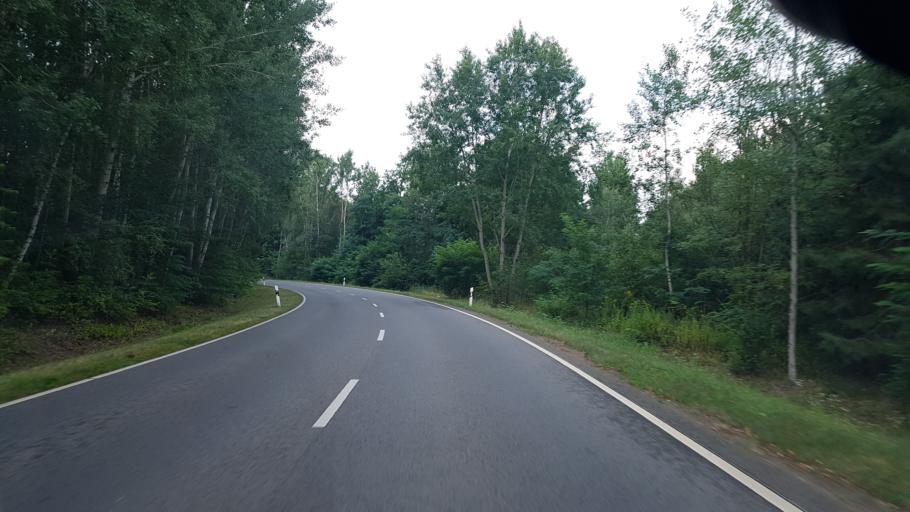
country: DE
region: Brandenburg
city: Lauchhammer
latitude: 51.4975
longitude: 13.7386
